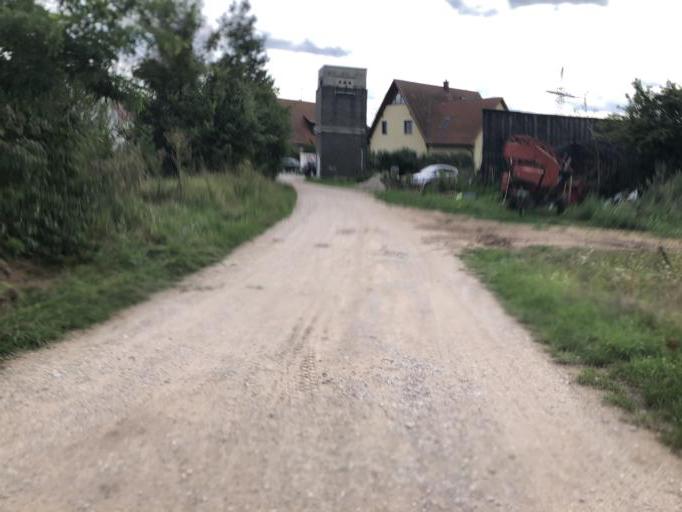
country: DE
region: Bavaria
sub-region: Regierungsbezirk Mittelfranken
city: Erlangen
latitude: 49.5360
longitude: 11.0020
